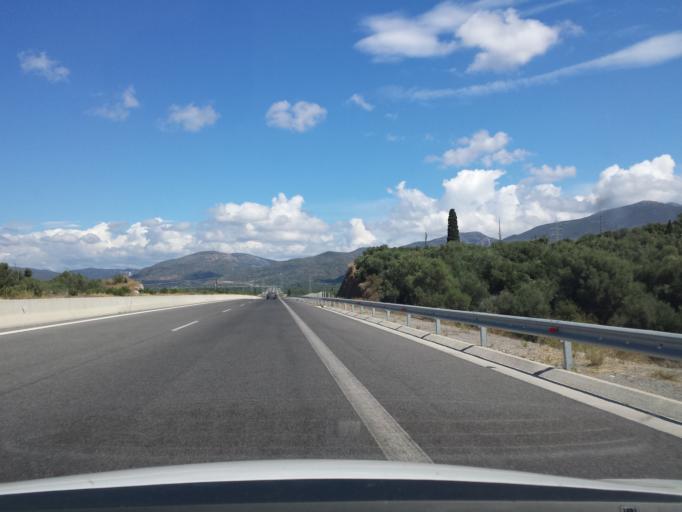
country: GR
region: Peloponnese
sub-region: Nomos Messinias
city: Meligalas
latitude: 37.2135
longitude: 22.0025
